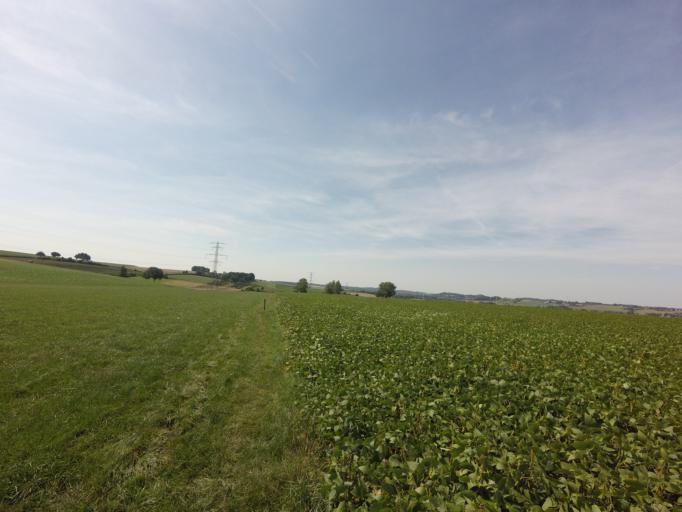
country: NL
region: Limburg
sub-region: Gemeente Voerendaal
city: Kunrade
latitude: 50.8575
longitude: 5.9074
